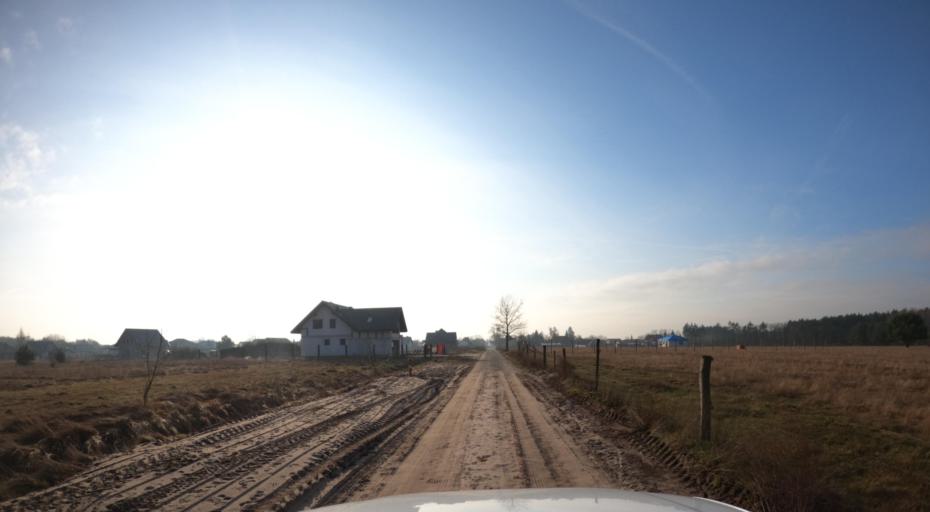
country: PL
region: Lubusz
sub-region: Powiat gorzowski
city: Kostrzyn nad Odra
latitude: 52.6188
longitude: 14.6243
